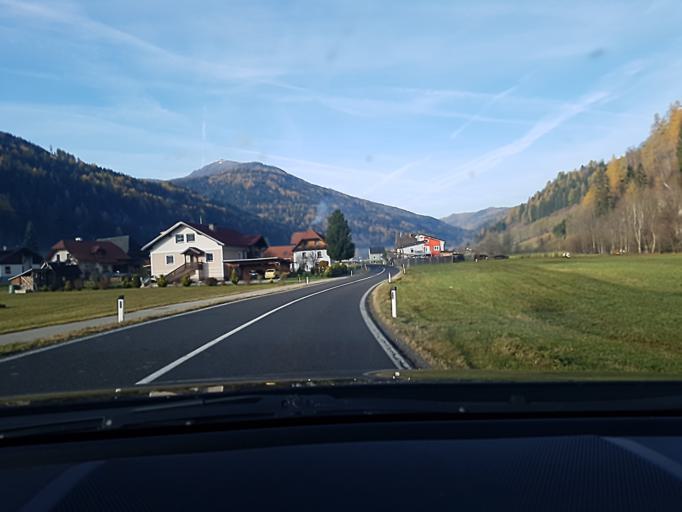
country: AT
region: Styria
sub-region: Politischer Bezirk Murau
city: Ranten
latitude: 47.1592
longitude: 14.0642
